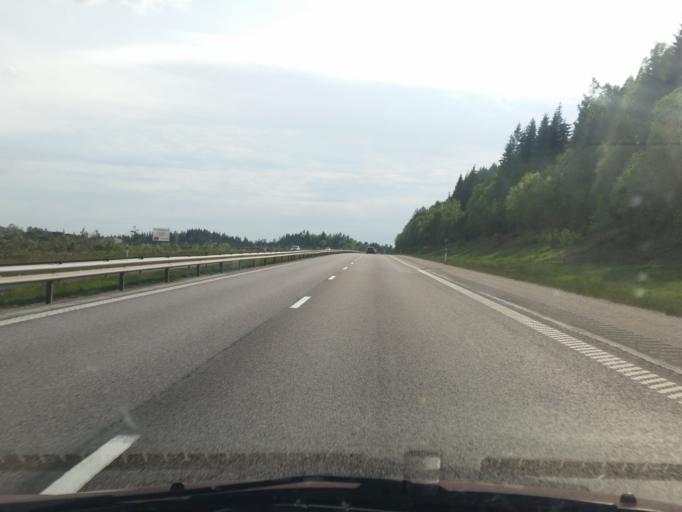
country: SE
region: Vaestra Goetaland
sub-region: Boras Kommun
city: Sandared
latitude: 57.6909
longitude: 12.7986
